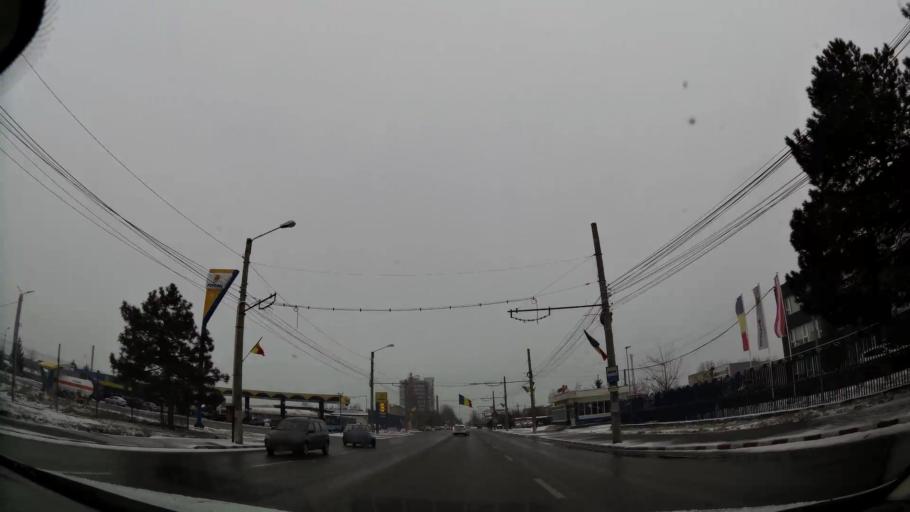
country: RO
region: Dambovita
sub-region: Municipiul Targoviste
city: Targoviste
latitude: 44.9132
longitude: 25.4507
